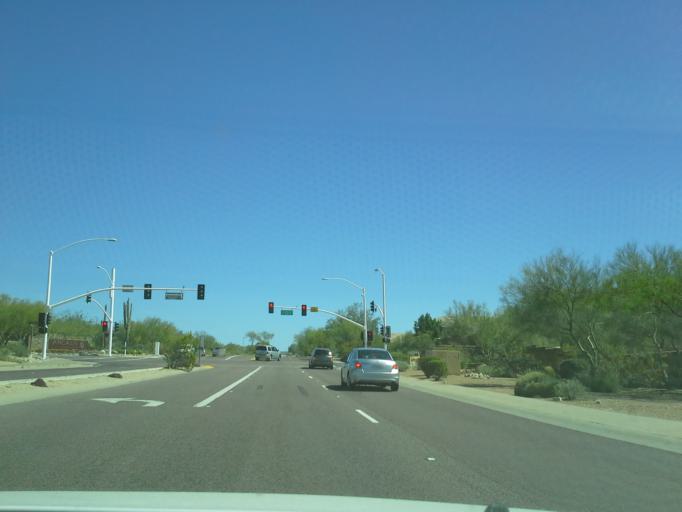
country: US
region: Arizona
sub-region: Maricopa County
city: Scottsdale
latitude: 33.5896
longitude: -111.8259
